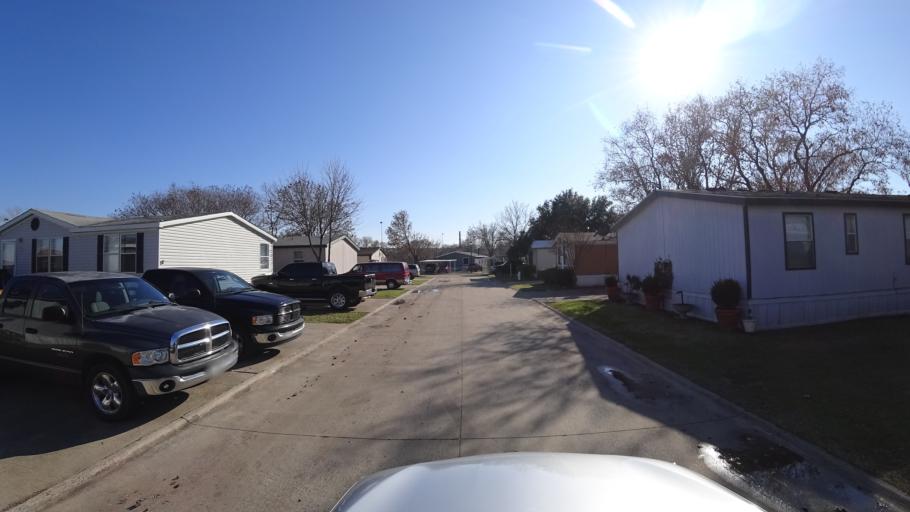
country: US
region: Texas
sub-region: Dallas County
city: Coppell
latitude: 32.9883
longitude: -97.0188
